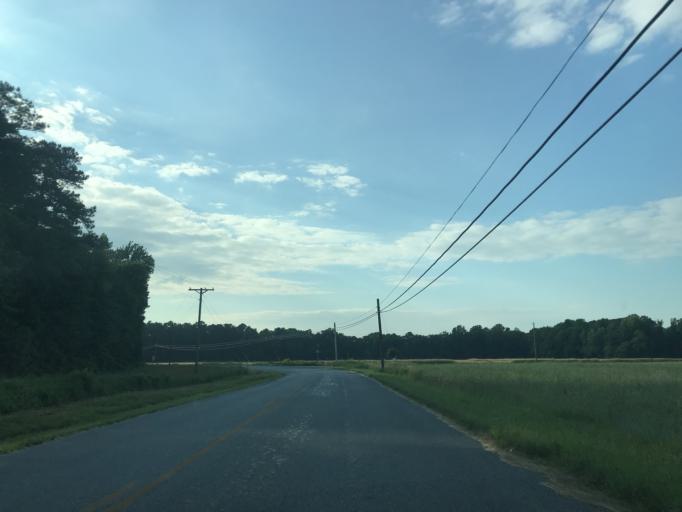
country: US
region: Maryland
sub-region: Caroline County
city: Federalsburg
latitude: 38.7207
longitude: -75.7815
